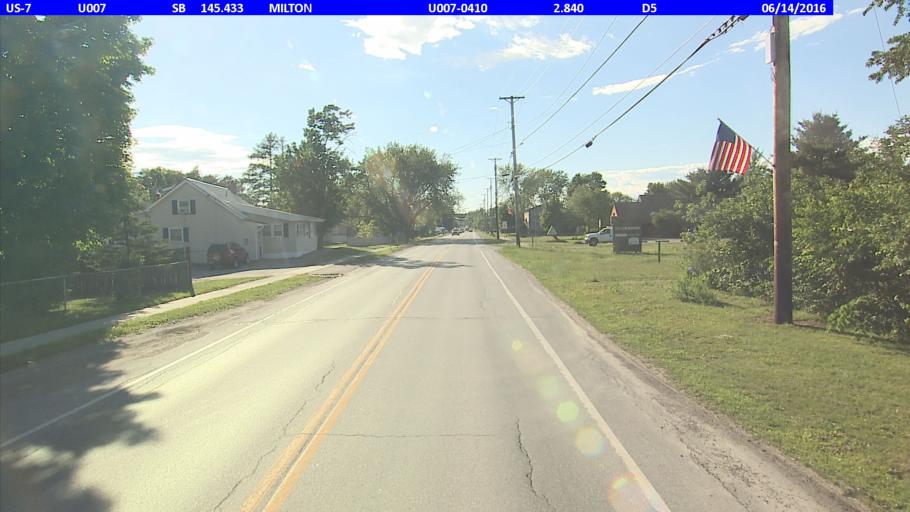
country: US
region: Vermont
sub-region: Chittenden County
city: Milton
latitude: 44.6256
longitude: -73.1373
